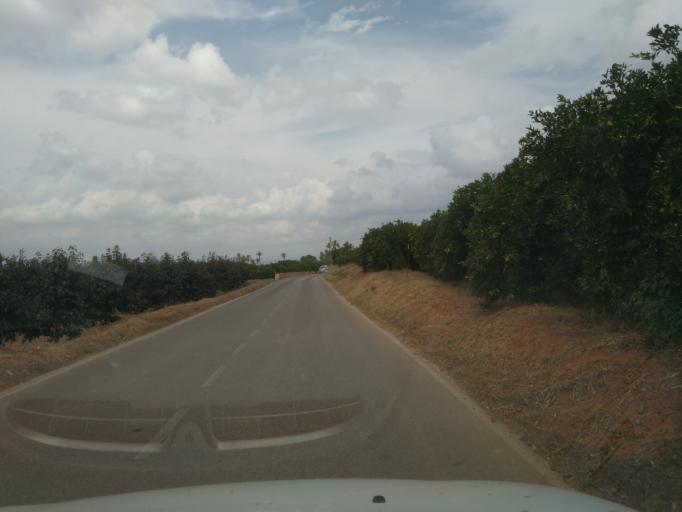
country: ES
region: Valencia
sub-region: Provincia de Valencia
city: La Pobla Llarga
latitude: 39.0904
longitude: -0.4275
